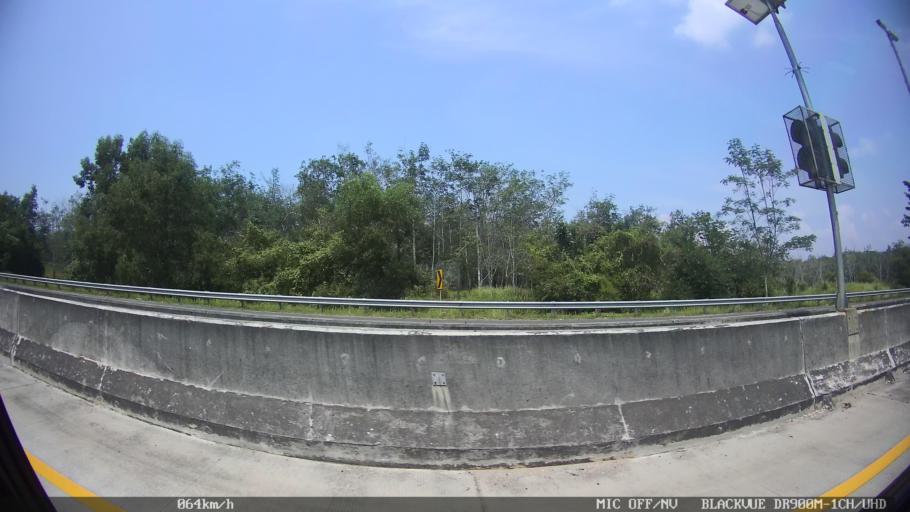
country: ID
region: Lampung
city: Kedaton
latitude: -5.3757
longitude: 105.3287
